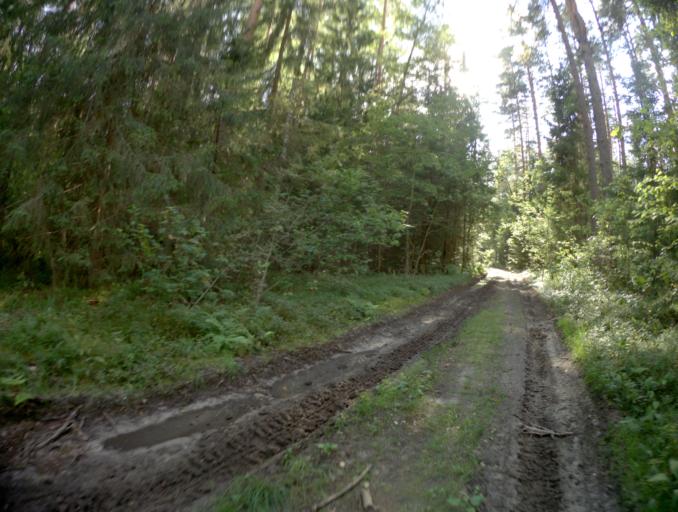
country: RU
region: Vladimir
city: Orgtrud
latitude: 56.1311
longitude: 40.5993
